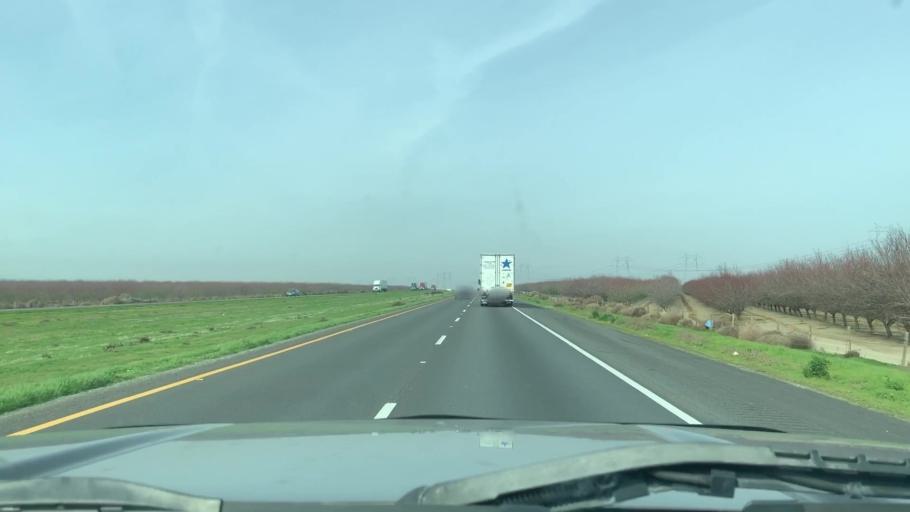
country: US
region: California
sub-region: Fresno County
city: Coalinga
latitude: 36.2763
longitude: -120.2576
